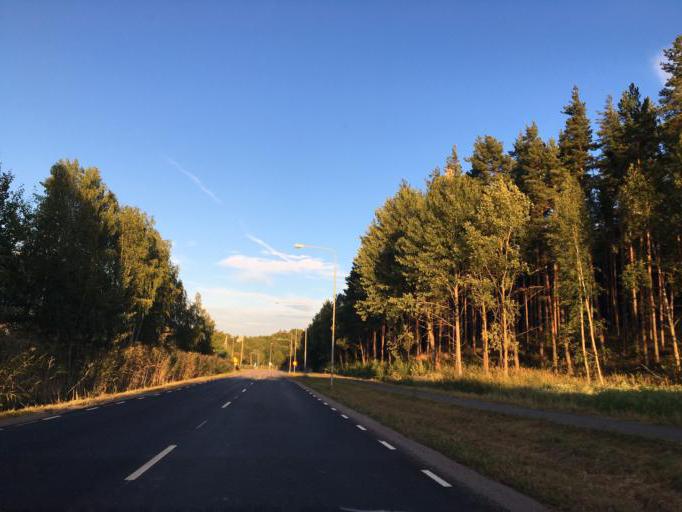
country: SE
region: Soedermanland
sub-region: Eskilstuna Kommun
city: Torshalla
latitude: 59.4284
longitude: 16.4552
